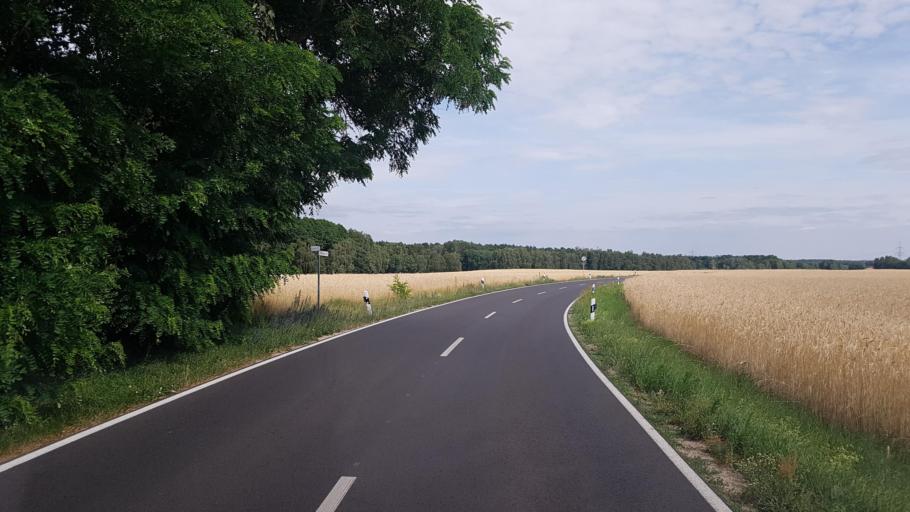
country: DE
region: Saxony-Anhalt
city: Abtsdorf
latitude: 51.9097
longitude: 12.6967
